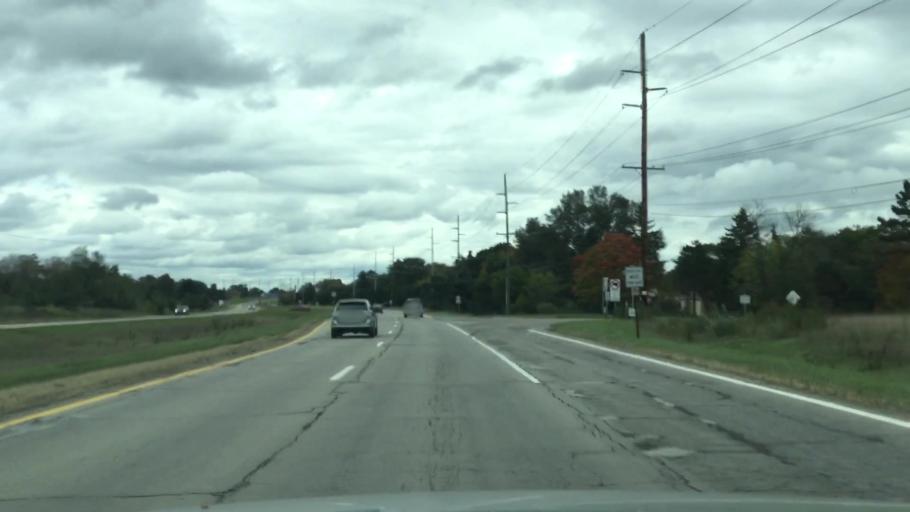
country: US
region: Michigan
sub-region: Oakland County
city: Milford
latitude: 42.6375
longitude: -83.6387
